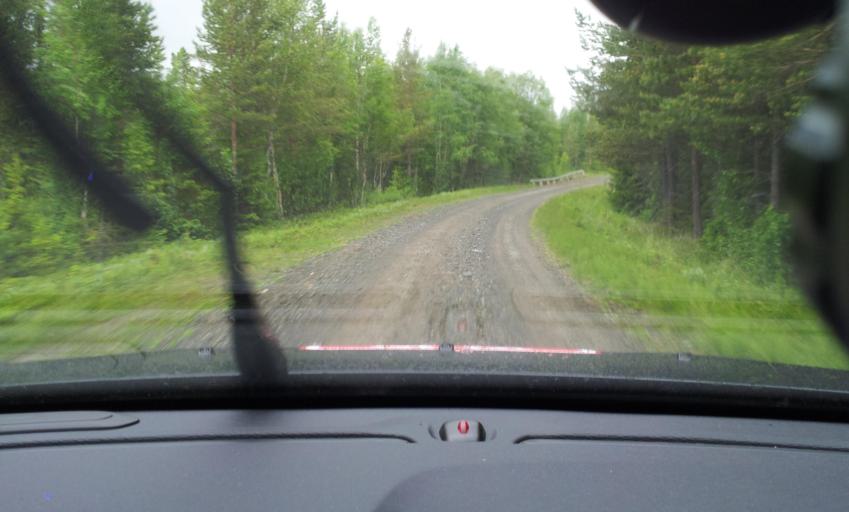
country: SE
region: Jaemtland
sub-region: Are Kommun
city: Are
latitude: 63.1876
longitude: 13.2055
